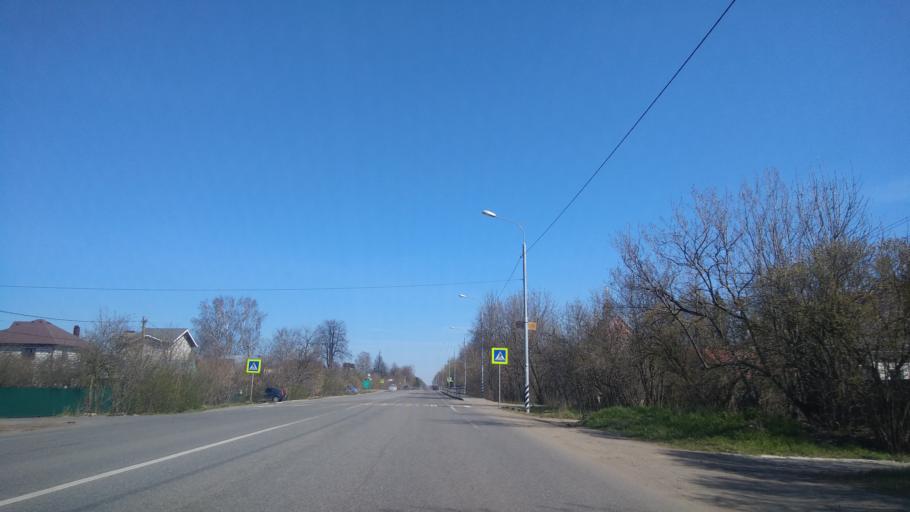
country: RU
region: Moskovskaya
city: Pushkino
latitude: 56.0204
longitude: 37.8716
